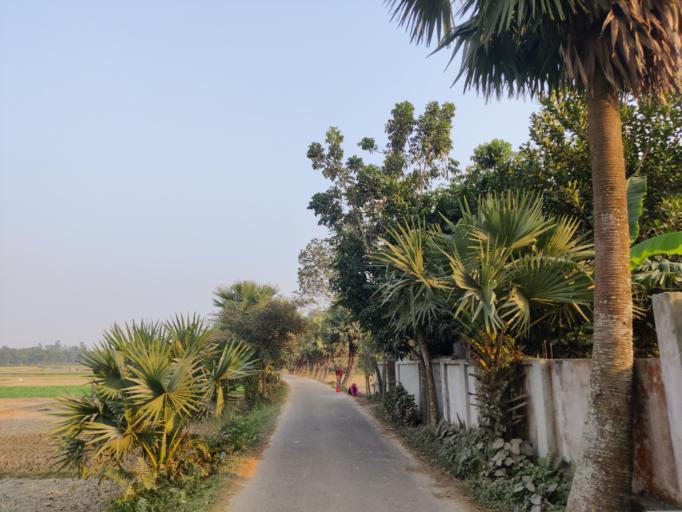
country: BD
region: Dhaka
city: Narsingdi
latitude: 24.0949
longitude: 90.7082
